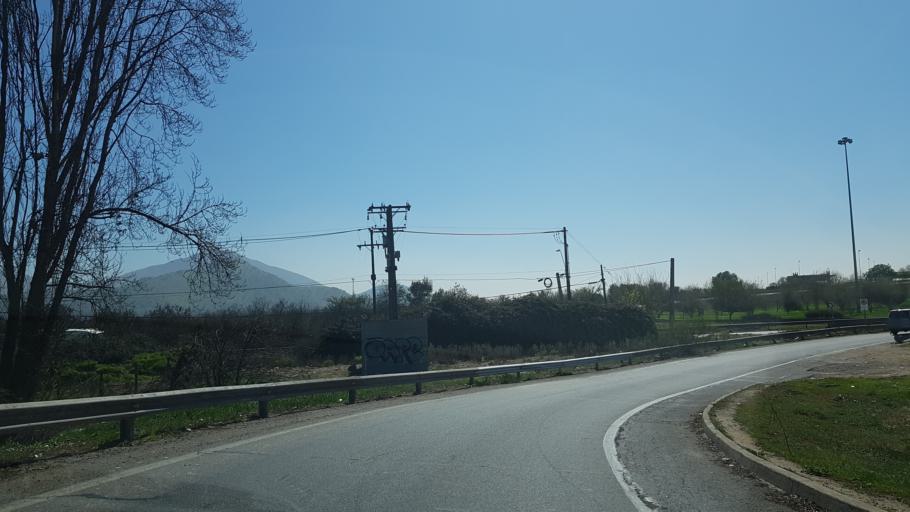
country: CL
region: Santiago Metropolitan
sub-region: Provincia de Santiago
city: Lo Prado
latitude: -33.5087
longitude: -70.8003
